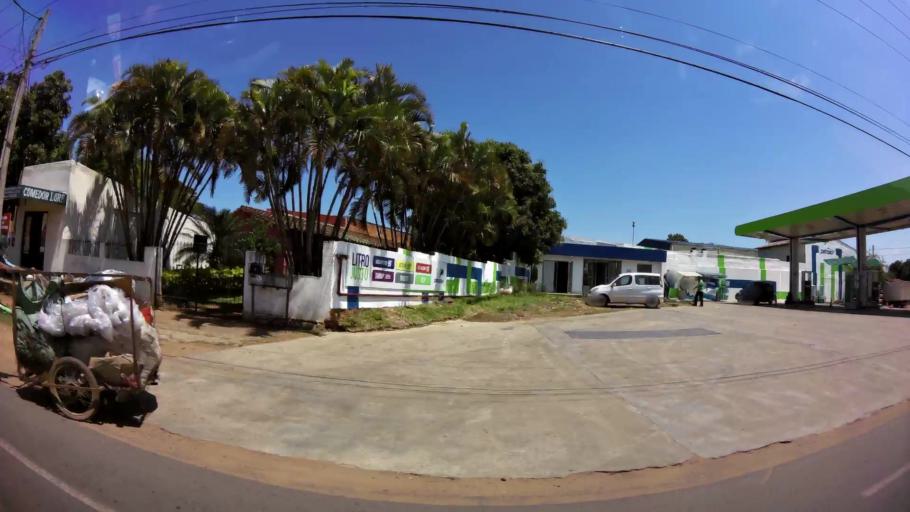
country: PY
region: Central
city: Nemby
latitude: -25.3753
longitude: -57.5178
